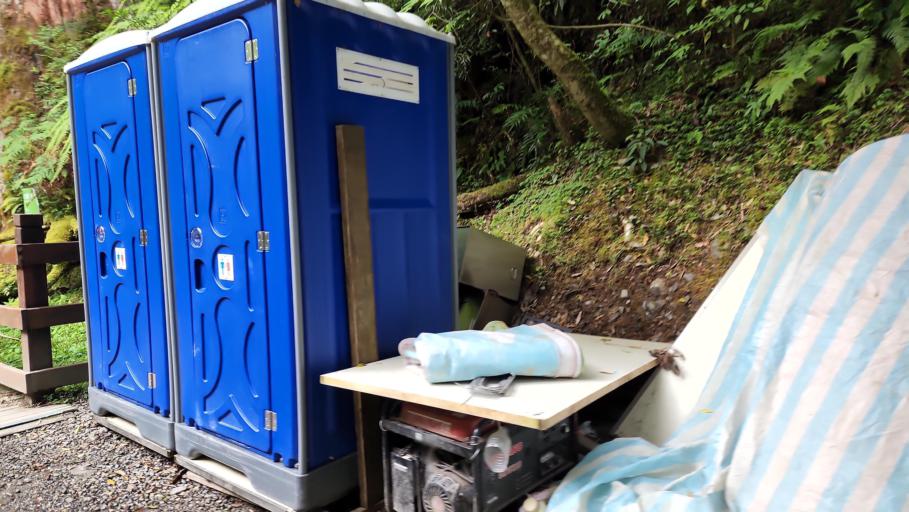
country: TW
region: Taiwan
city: Daxi
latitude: 24.7099
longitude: 121.4399
